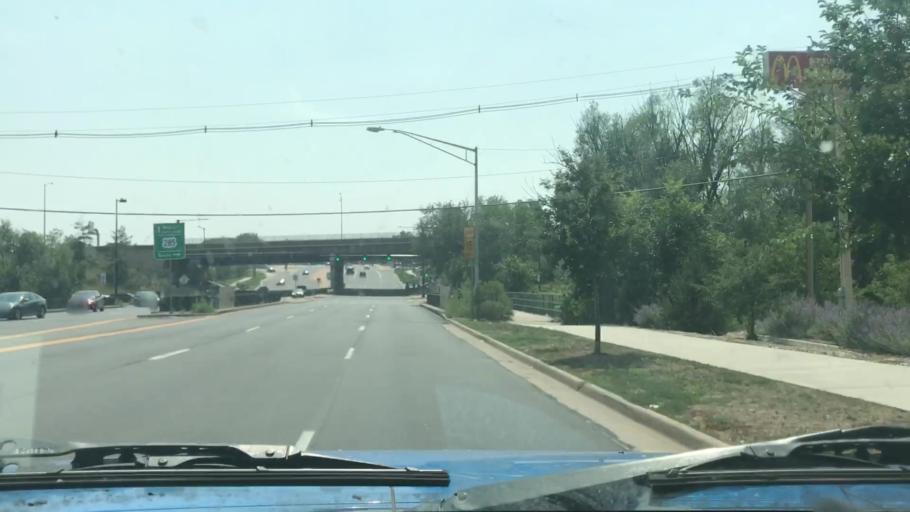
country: US
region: Colorado
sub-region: Arapahoe County
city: Sheridan
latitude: 39.6549
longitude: -105.0534
